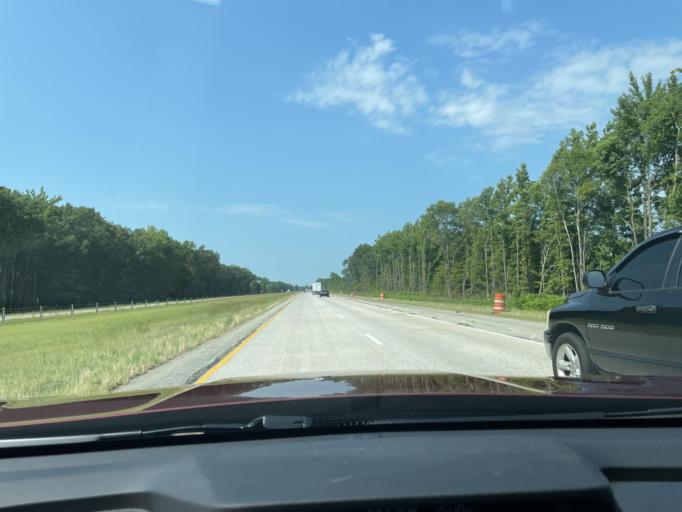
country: US
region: Arkansas
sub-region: White County
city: Searcy
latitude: 35.1602
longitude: -91.7819
